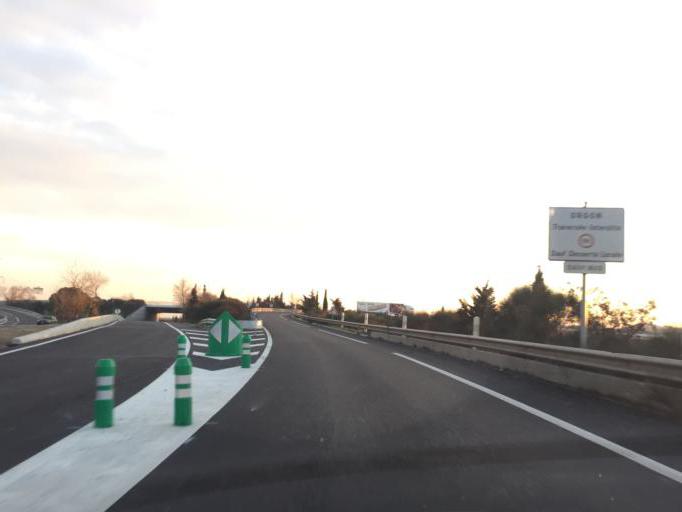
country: FR
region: Provence-Alpes-Cote d'Azur
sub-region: Departement du Vaucluse
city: Cavaillon
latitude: 43.8247
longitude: 5.0283
